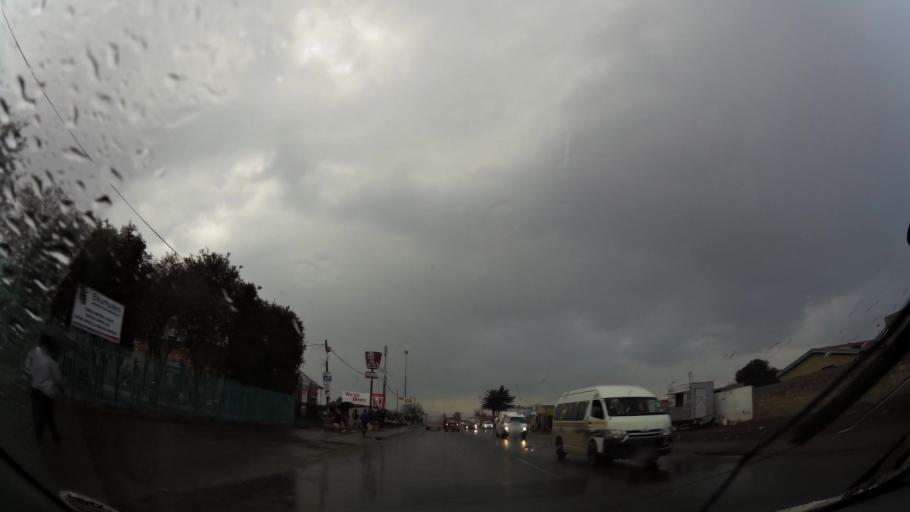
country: ZA
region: Gauteng
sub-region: Ekurhuleni Metropolitan Municipality
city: Germiston
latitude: -26.3552
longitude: 28.1311
